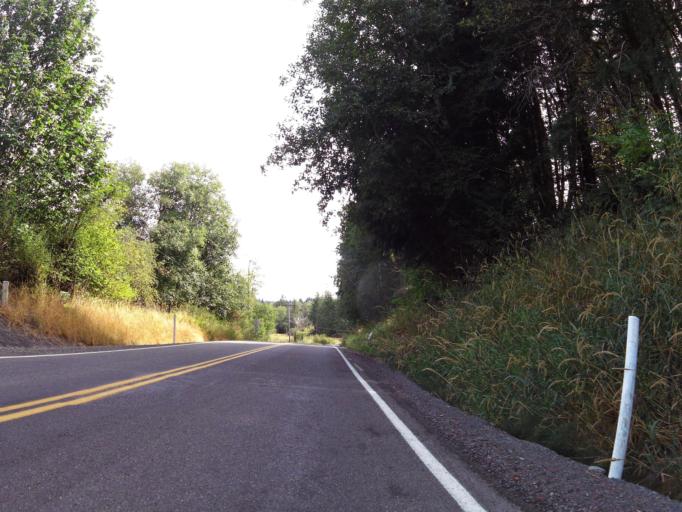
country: US
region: Washington
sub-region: Lewis County
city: Napavine
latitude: 46.5614
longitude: -122.9641
